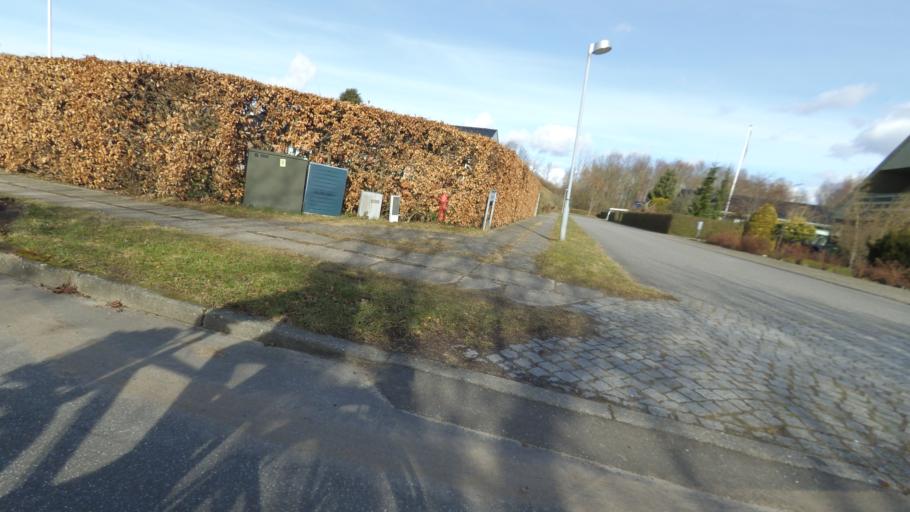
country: DK
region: Central Jutland
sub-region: Arhus Kommune
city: Tranbjerg
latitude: 56.0905
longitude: 10.1259
